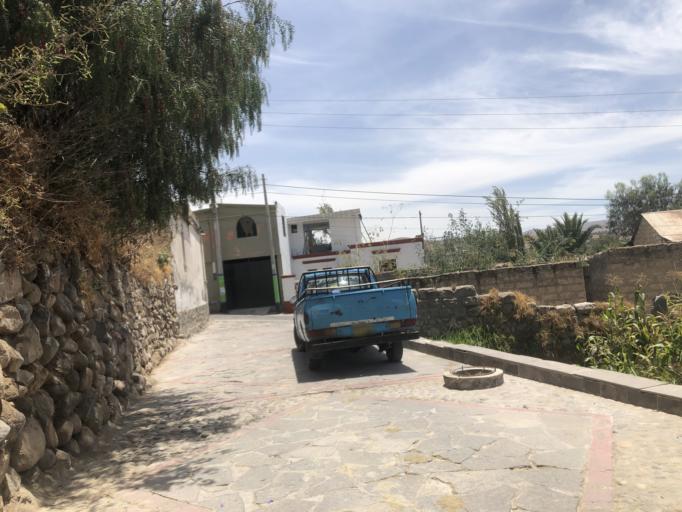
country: PE
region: Arequipa
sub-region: Provincia de Arequipa
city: Quequena
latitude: -16.5566
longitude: -71.4530
